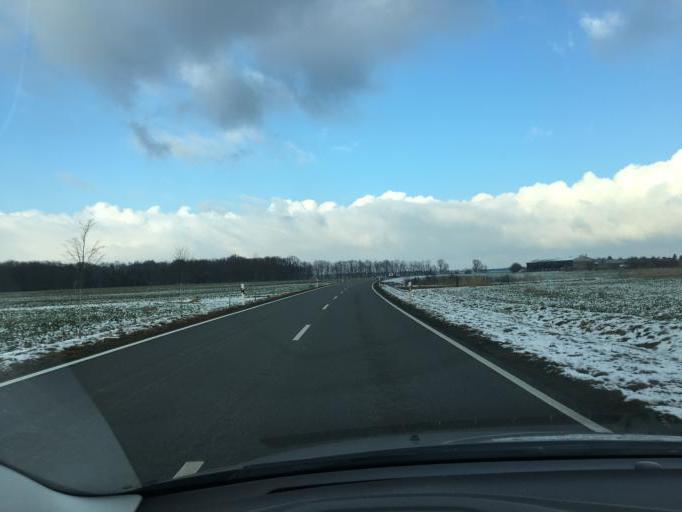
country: DE
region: Saxony
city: Brandis
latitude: 51.3348
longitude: 12.5913
